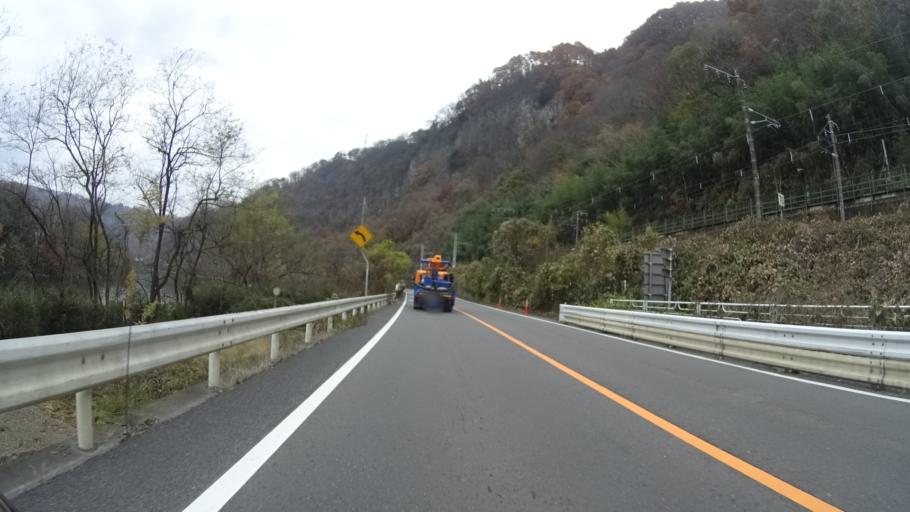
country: JP
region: Gunma
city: Numata
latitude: 36.5944
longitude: 139.0491
